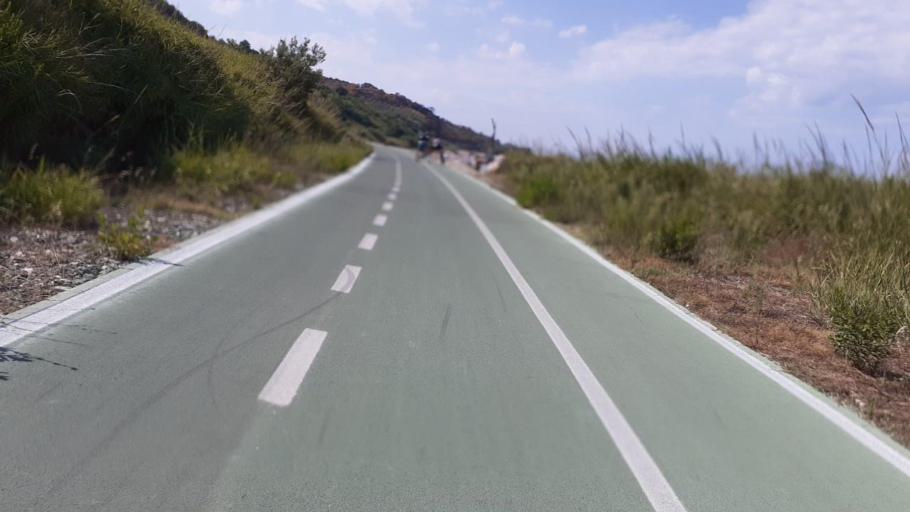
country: IT
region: Abruzzo
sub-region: Provincia di Chieti
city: Fossacesia
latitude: 42.2731
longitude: 14.5002
